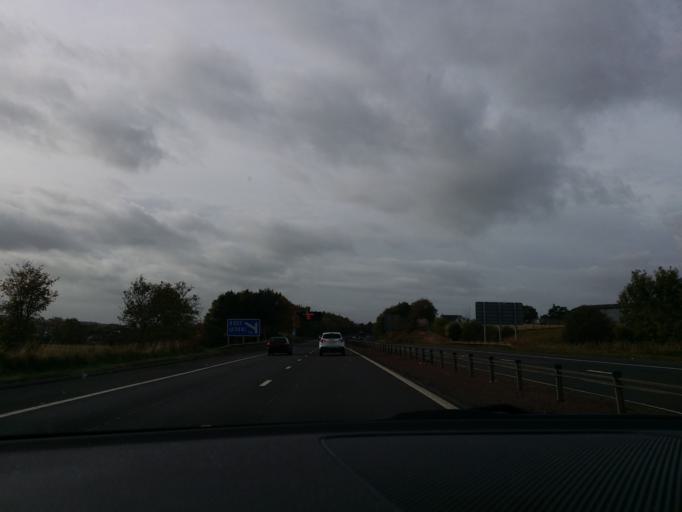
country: GB
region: Scotland
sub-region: Fife
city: Limekilns
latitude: 55.9832
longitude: -3.5277
